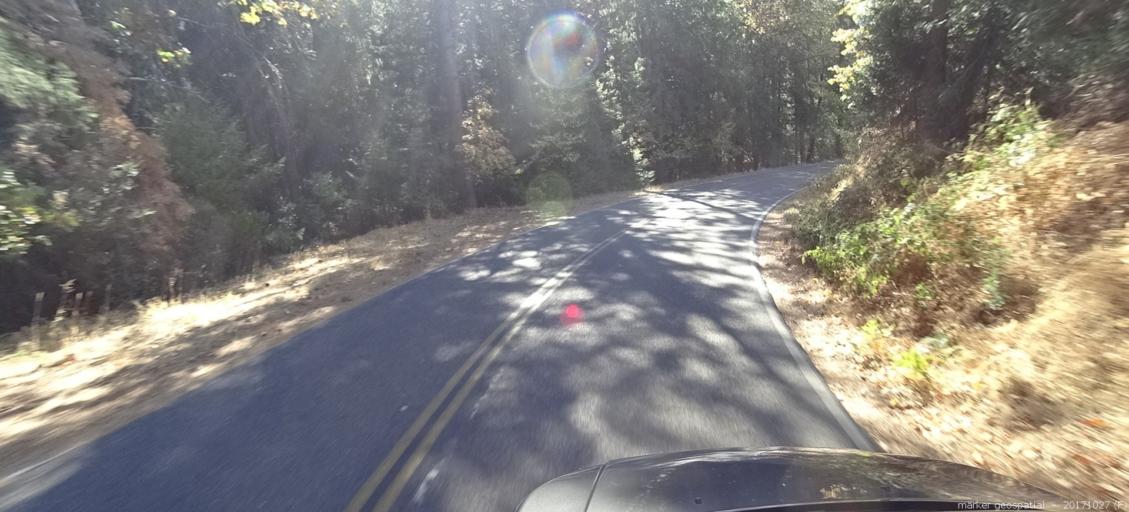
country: US
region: California
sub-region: Shasta County
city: Shingletown
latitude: 40.6928
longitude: -121.9287
